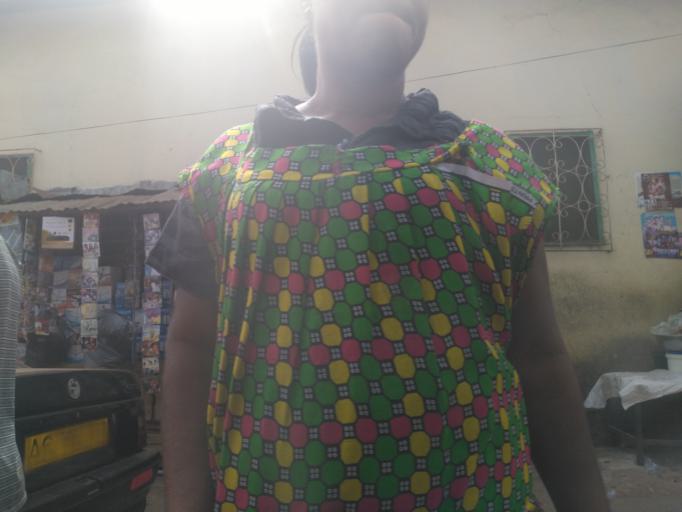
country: GH
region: Ashanti
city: Kumasi
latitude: 6.6996
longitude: -1.6202
